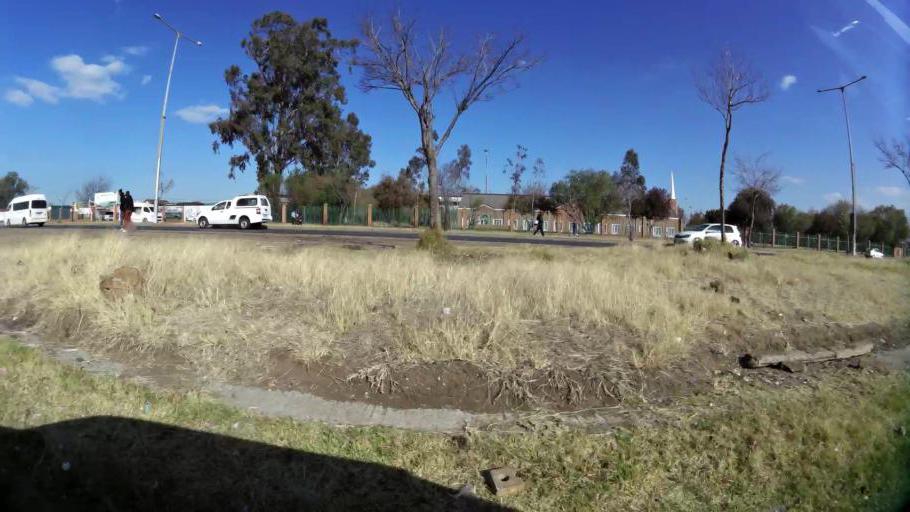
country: ZA
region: Gauteng
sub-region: City of Johannesburg Metropolitan Municipality
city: Soweto
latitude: -26.2599
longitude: 27.9065
